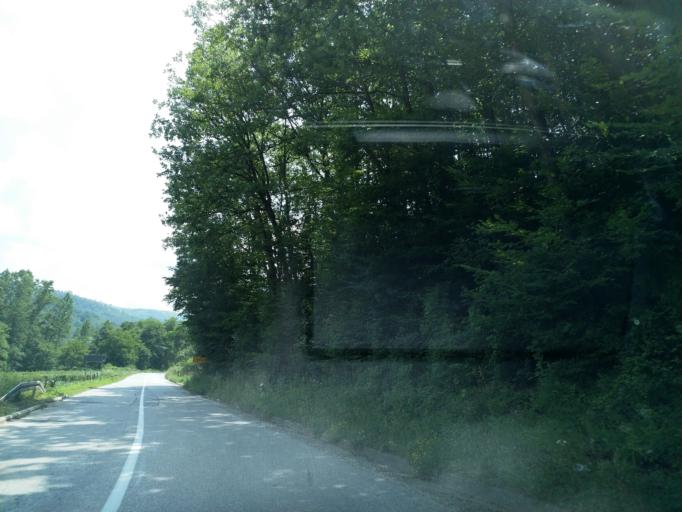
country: RS
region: Central Serbia
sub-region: Rasinski Okrug
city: Aleksandrovac
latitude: 43.3659
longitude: 20.9943
